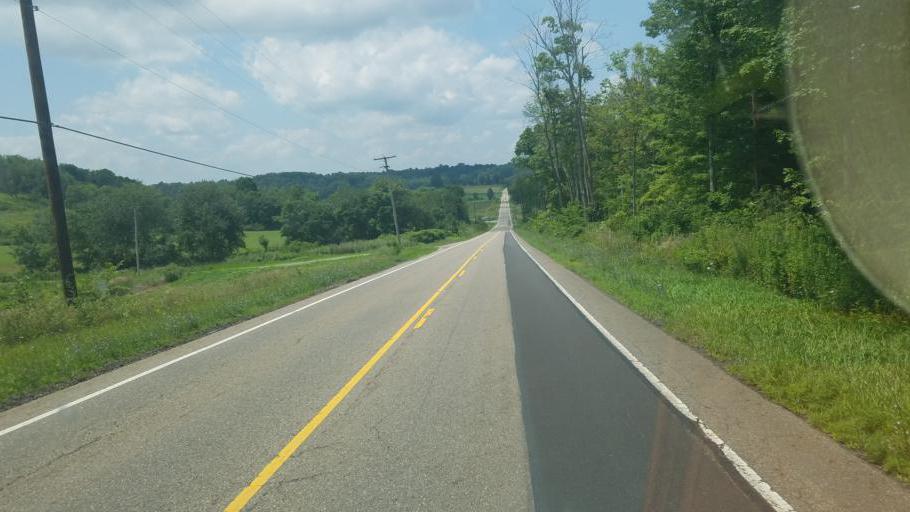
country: US
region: Ohio
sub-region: Stark County
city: Minerva
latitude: 40.7928
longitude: -81.1145
